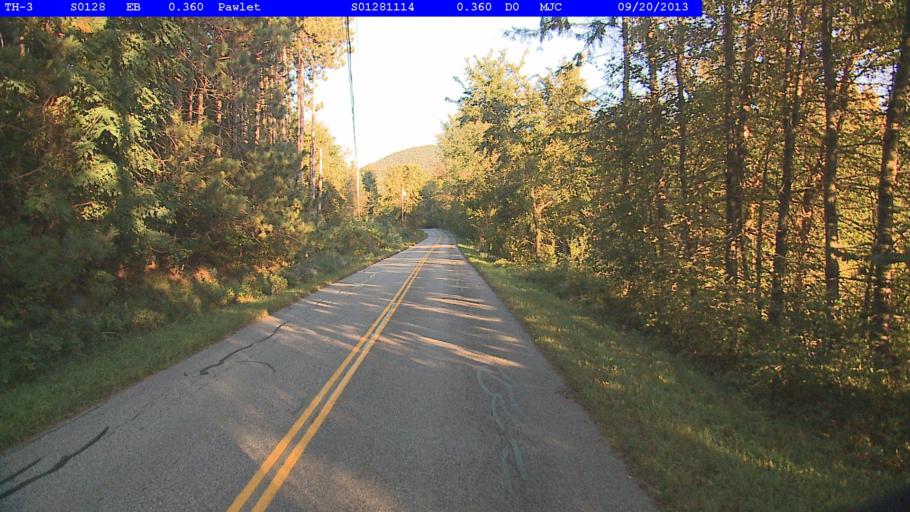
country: US
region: New York
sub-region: Washington County
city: Granville
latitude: 43.3719
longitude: -73.2231
